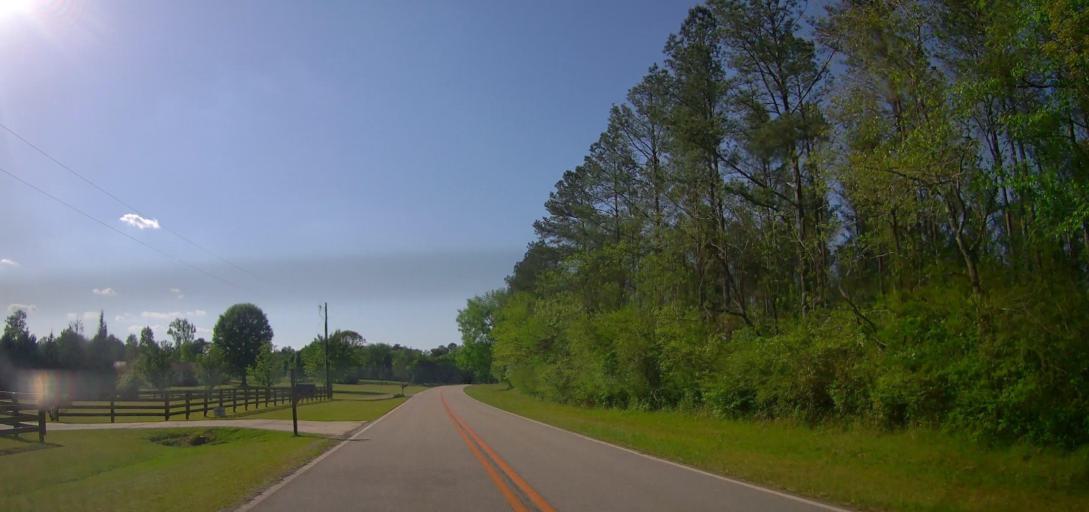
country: US
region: Georgia
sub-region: Morgan County
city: Madison
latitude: 33.5190
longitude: -83.5047
